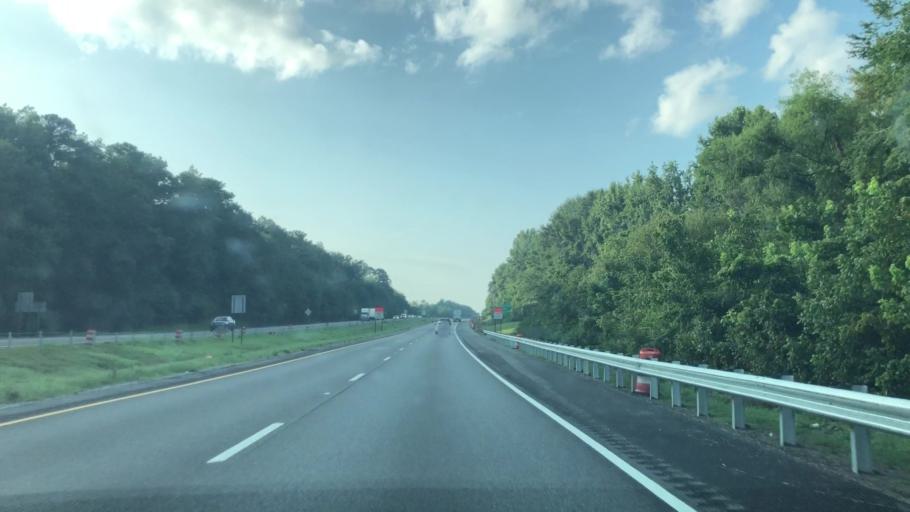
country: US
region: Alabama
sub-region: Chilton County
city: Clanton
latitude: 32.8569
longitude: -86.6014
